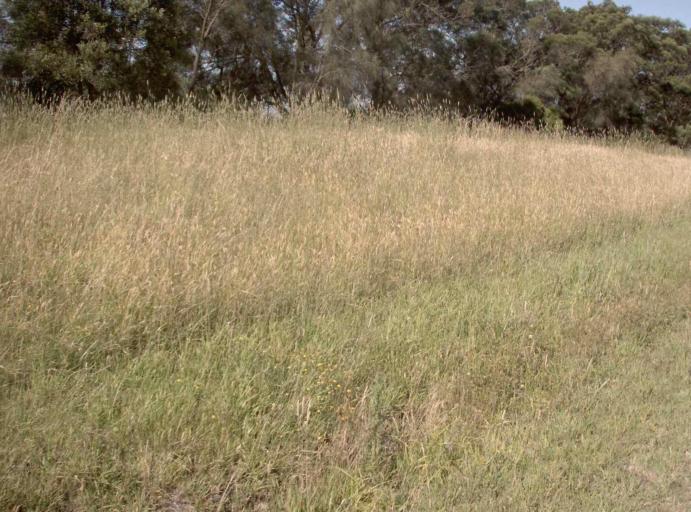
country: AU
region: Victoria
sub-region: Latrobe
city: Traralgon
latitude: -38.6256
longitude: 146.6513
